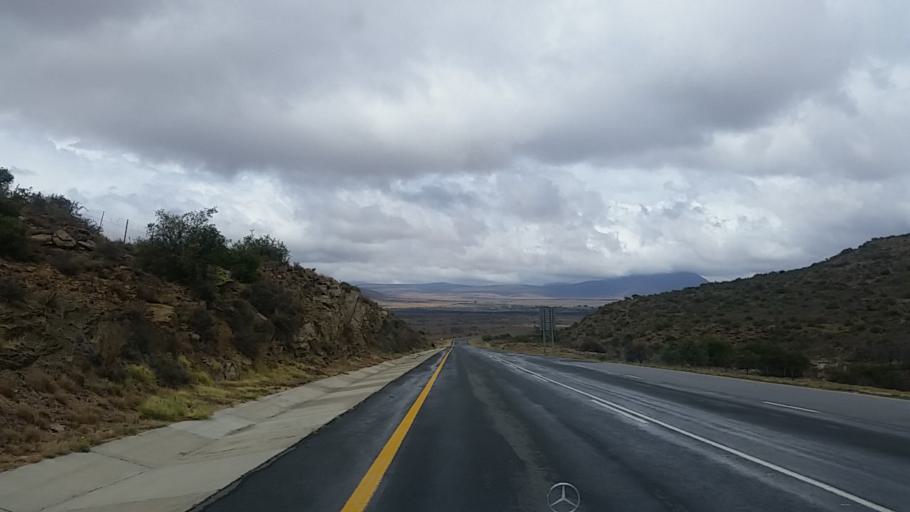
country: ZA
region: Eastern Cape
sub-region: Cacadu District Municipality
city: Graaff-Reinet
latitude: -32.1422
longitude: 24.5769
